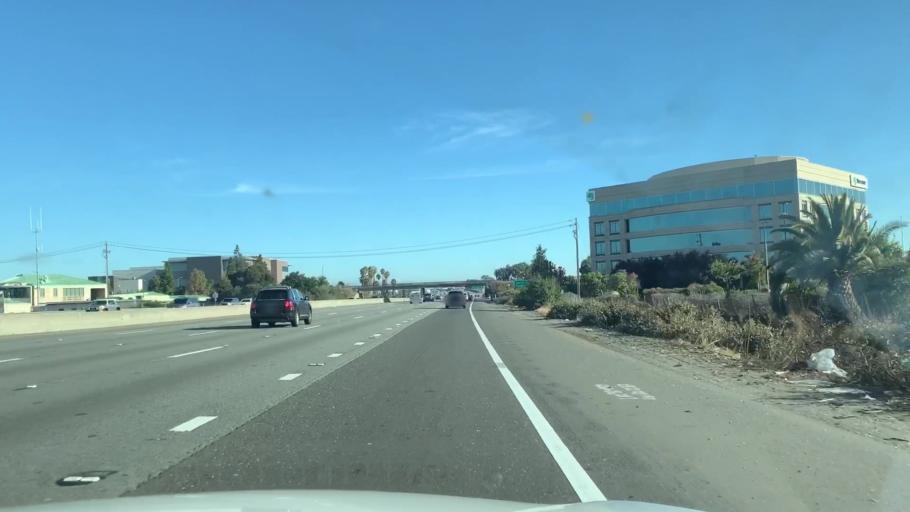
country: US
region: California
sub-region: San Mateo County
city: Redwood City
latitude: 37.4930
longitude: -122.2237
